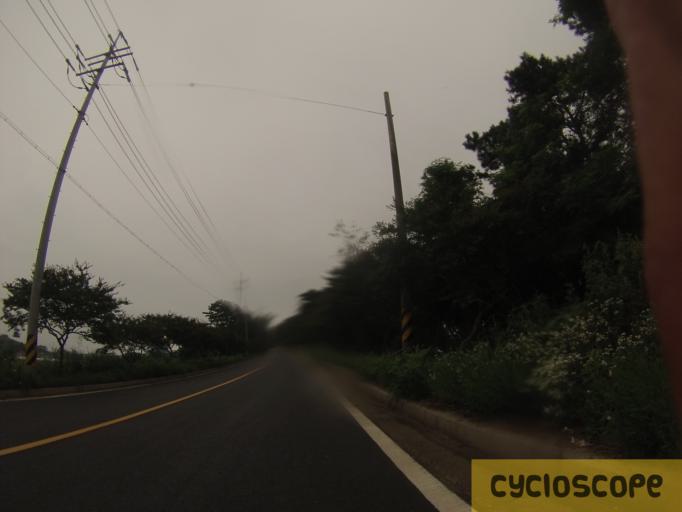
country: KR
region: Chungcheongnam-do
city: Taisen-ri
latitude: 36.2100
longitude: 126.5584
